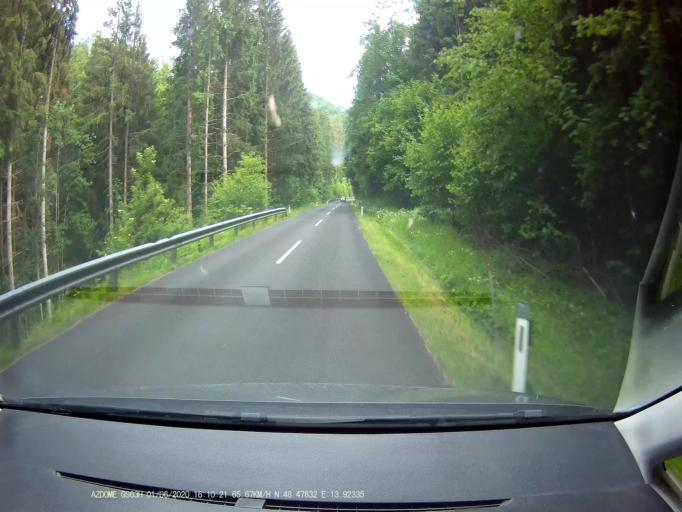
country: AT
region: Upper Austria
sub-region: Politischer Bezirk Rohrbach
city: Atzesberg
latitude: 48.4781
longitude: 13.9236
